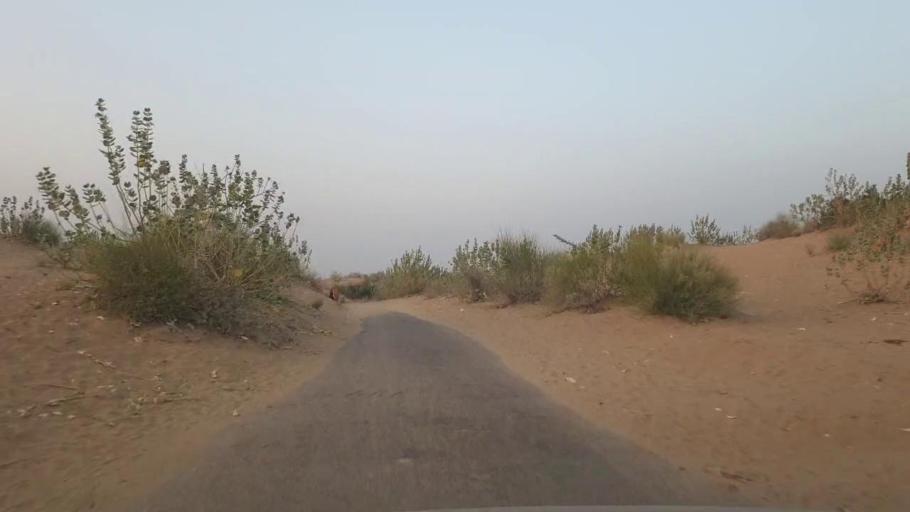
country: PK
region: Sindh
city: Umarkot
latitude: 25.2874
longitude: 70.0782
